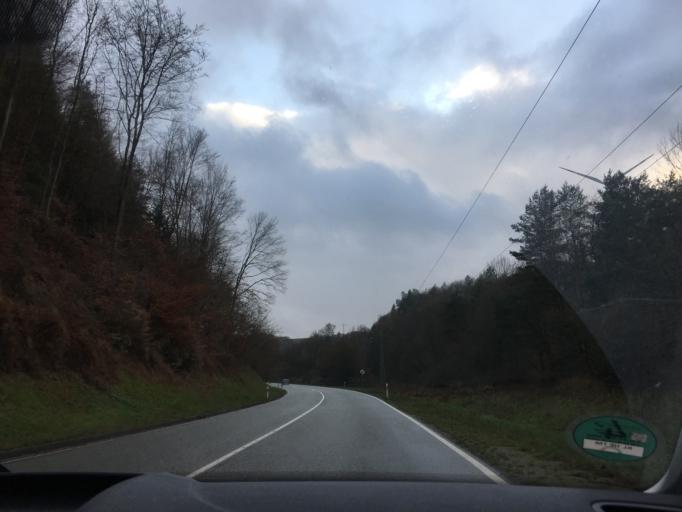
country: DE
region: Rheinland-Pfalz
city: Donsieders
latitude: 49.2496
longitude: 7.6025
